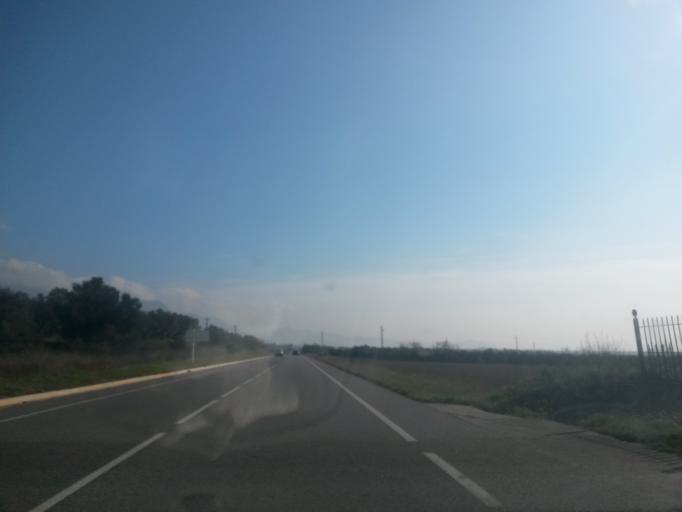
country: ES
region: Catalonia
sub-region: Provincia de Girona
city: Vilajuiga
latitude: 42.3220
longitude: 3.0953
